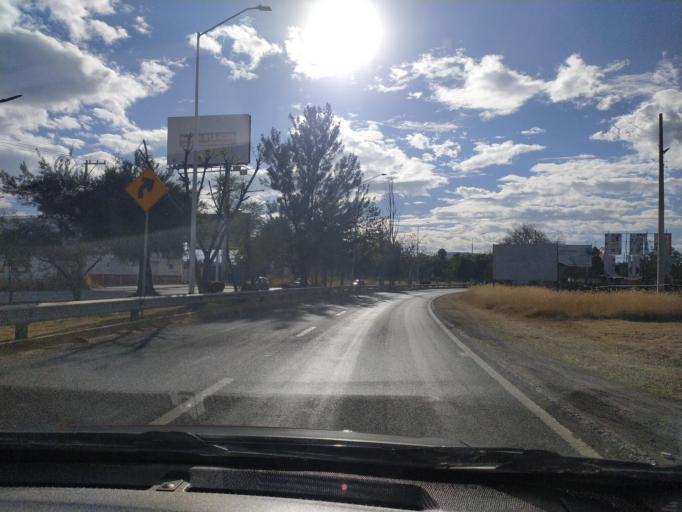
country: LA
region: Oudomxai
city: Muang La
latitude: 21.0316
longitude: 101.8316
